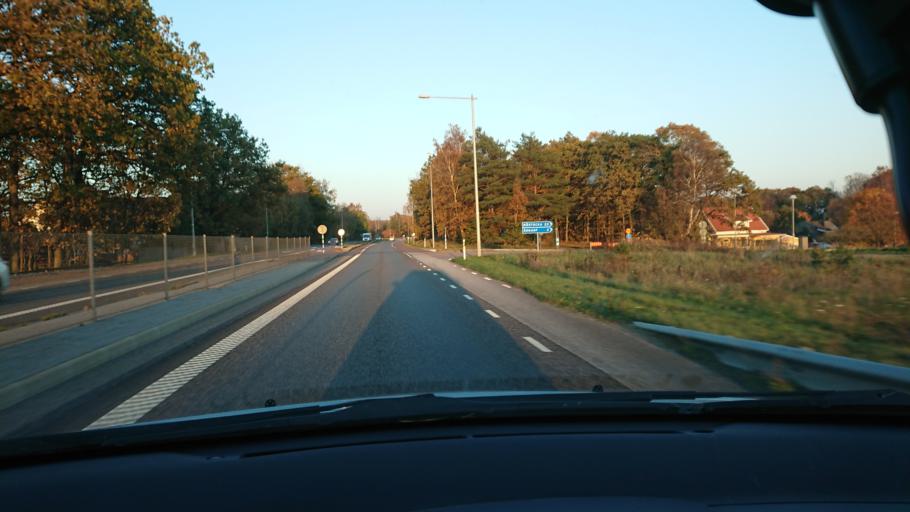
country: SE
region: Halland
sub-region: Halmstads Kommun
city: Aled
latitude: 56.6926
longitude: 12.9729
